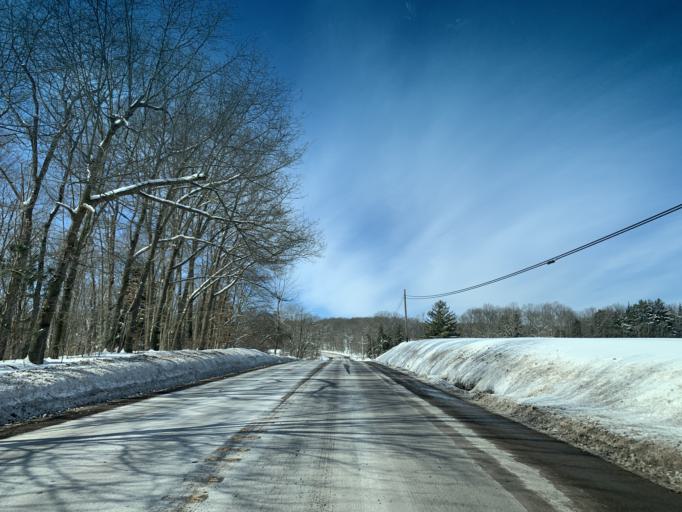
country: US
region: Pennsylvania
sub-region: Somerset County
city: Meyersdale
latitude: 39.7022
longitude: -79.1859
